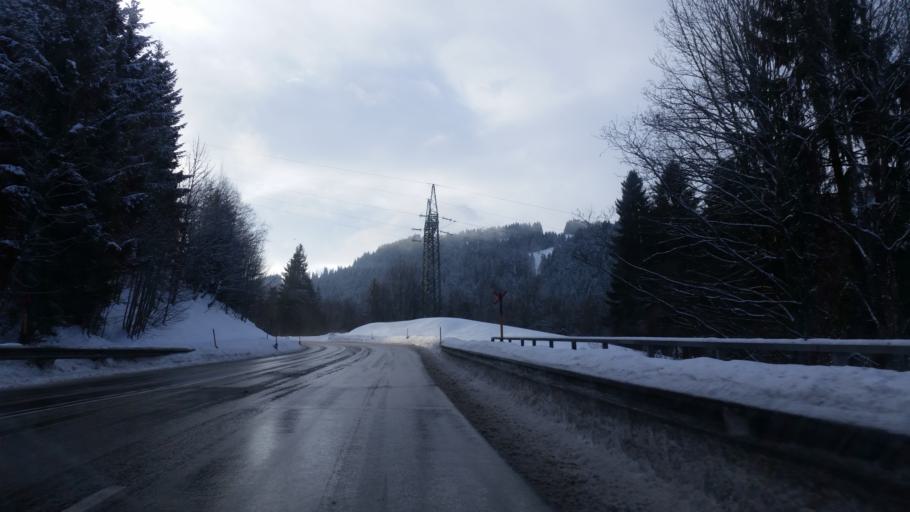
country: AT
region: Tyrol
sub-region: Politischer Bezirk Kitzbuhel
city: Fieberbrunn
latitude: 47.4705
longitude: 12.5643
